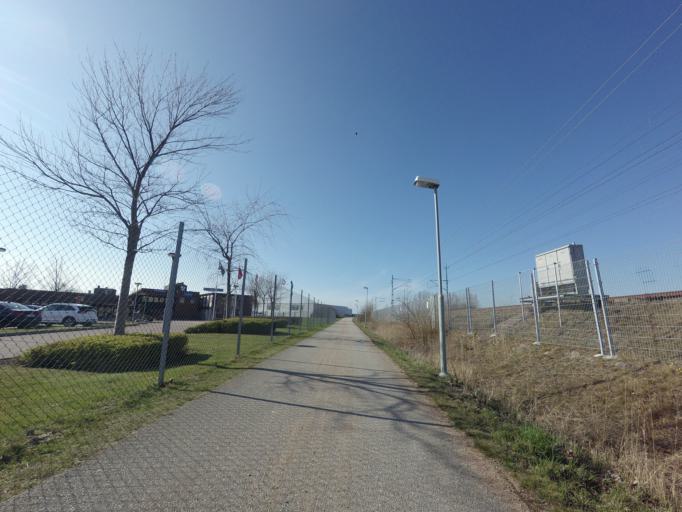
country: SE
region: Skane
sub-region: Landskrona
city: Landskrona
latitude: 55.8722
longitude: 12.8635
